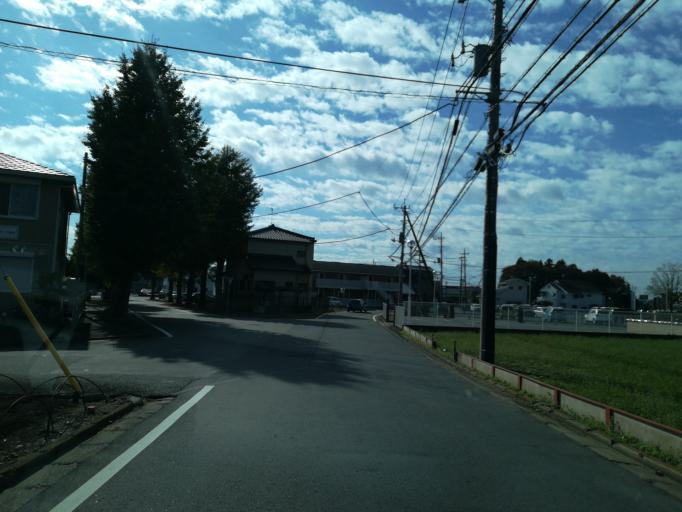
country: JP
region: Ibaraki
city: Naka
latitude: 36.0728
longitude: 140.0924
